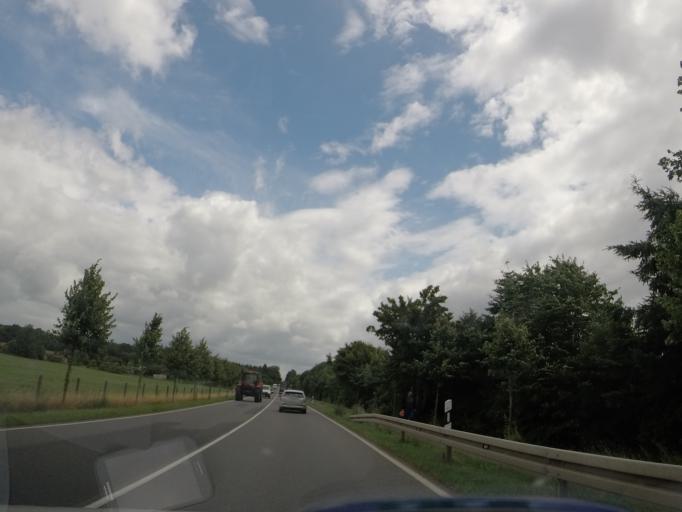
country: DE
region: Mecklenburg-Vorpommern
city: Lalendorf
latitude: 53.7590
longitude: 12.3803
